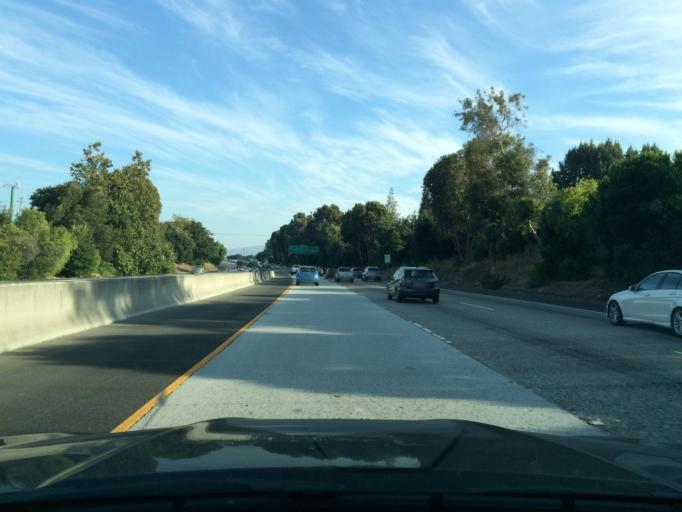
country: US
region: California
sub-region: Santa Clara County
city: Sunnyvale
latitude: 37.3582
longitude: -122.0629
